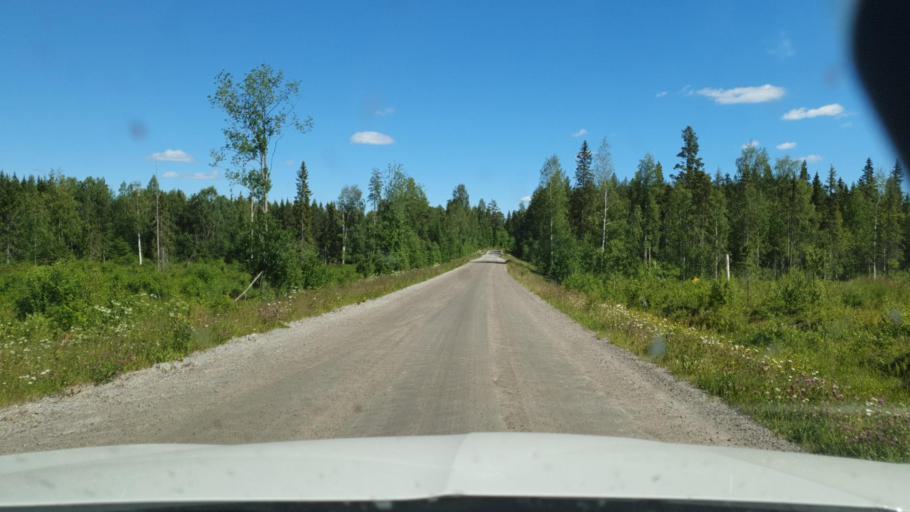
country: SE
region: Vaesterbotten
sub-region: Skelleftea Kommun
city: Byske
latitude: 65.1050
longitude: 21.1752
